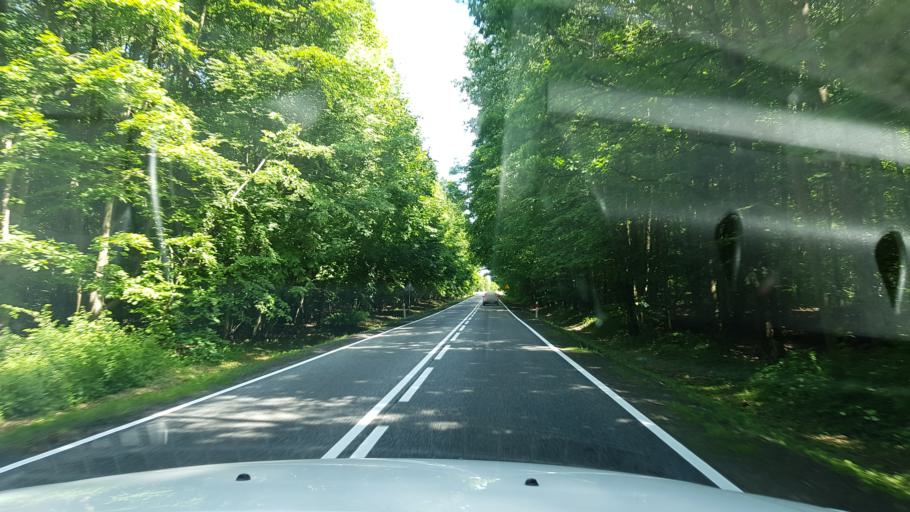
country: PL
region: West Pomeranian Voivodeship
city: Trzcinsko Zdroj
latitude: 52.9611
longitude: 14.5174
